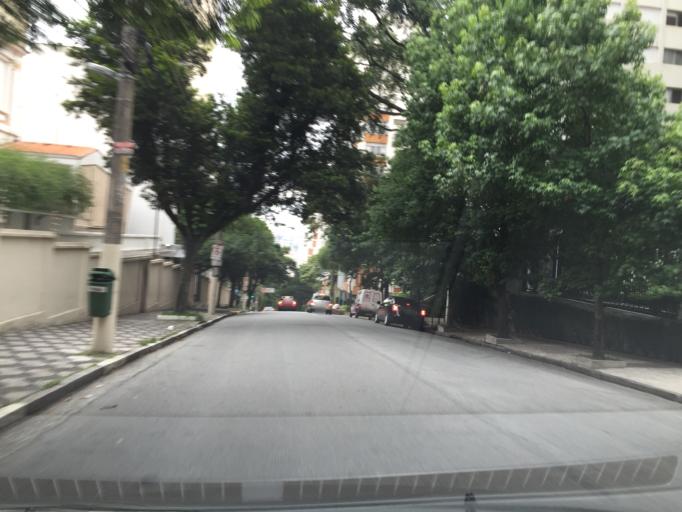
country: BR
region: Sao Paulo
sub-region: Sao Paulo
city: Sao Paulo
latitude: -23.5628
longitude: -46.6591
